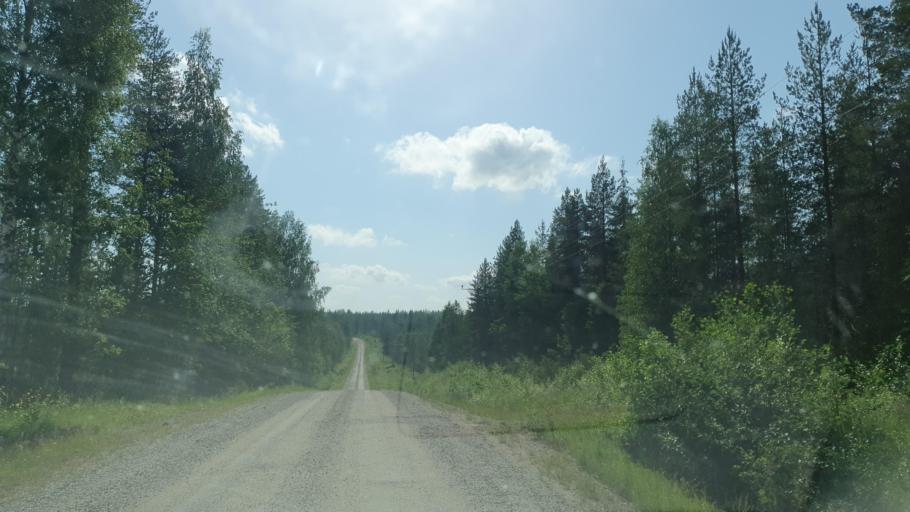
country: FI
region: Kainuu
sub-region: Kehys-Kainuu
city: Kuhmo
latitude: 64.0364
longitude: 29.9403
